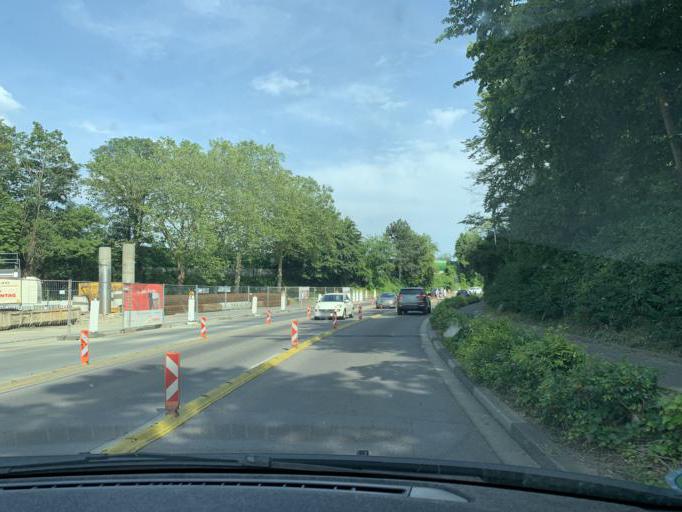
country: DE
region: North Rhine-Westphalia
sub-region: Regierungsbezirk Dusseldorf
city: Viersen
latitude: 51.2620
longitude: 6.3927
